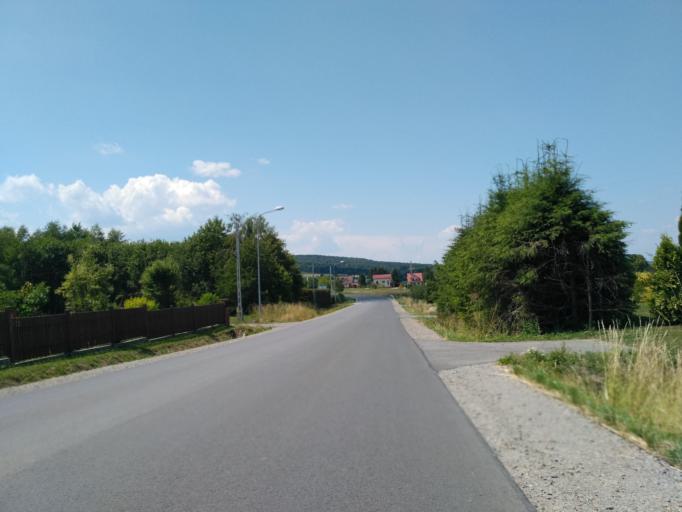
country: PL
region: Subcarpathian Voivodeship
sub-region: Powiat sanocki
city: Strachocina
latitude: 49.5730
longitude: 22.1414
